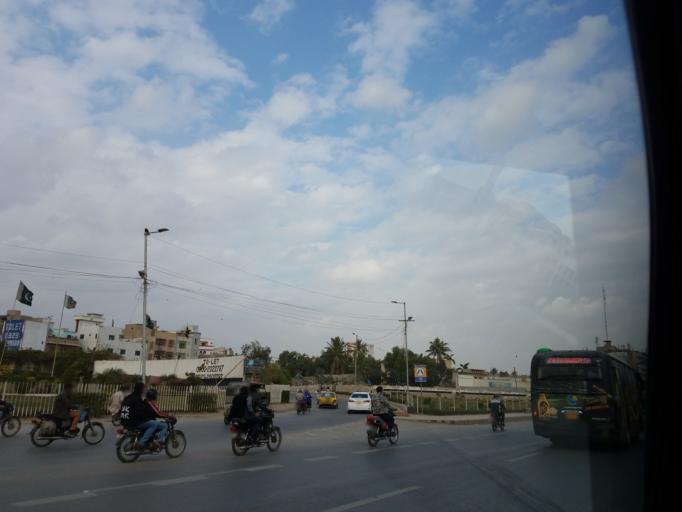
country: PK
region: Sindh
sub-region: Karachi District
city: Karachi
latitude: 24.8586
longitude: 67.0506
